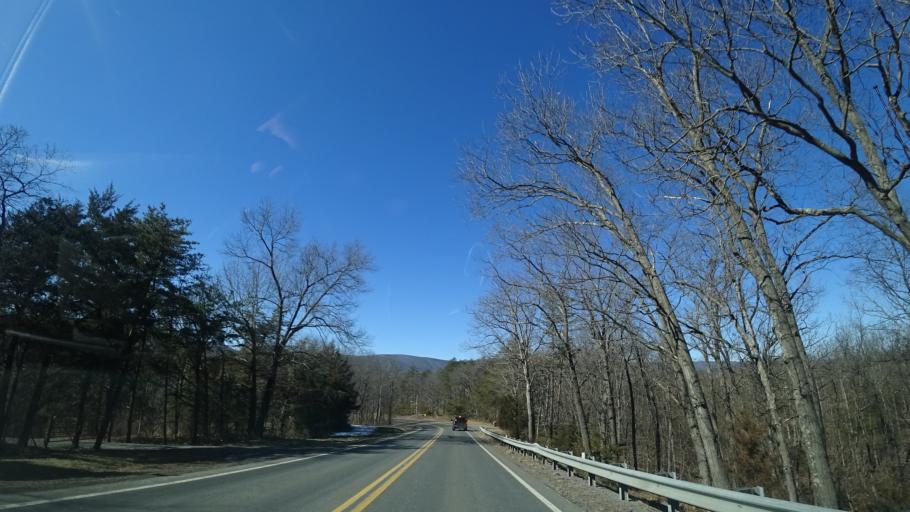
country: US
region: Virginia
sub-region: Shenandoah County
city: Strasburg
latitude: 39.0745
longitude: -78.4112
